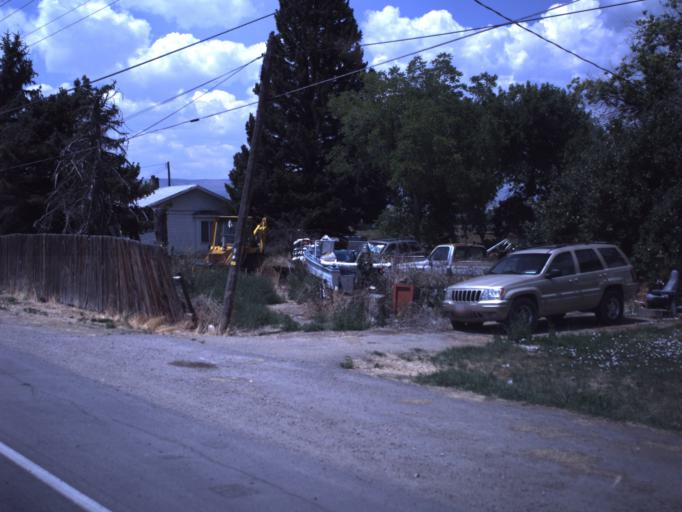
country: US
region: Utah
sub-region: Uintah County
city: Vernal
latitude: 40.4629
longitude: -109.5426
